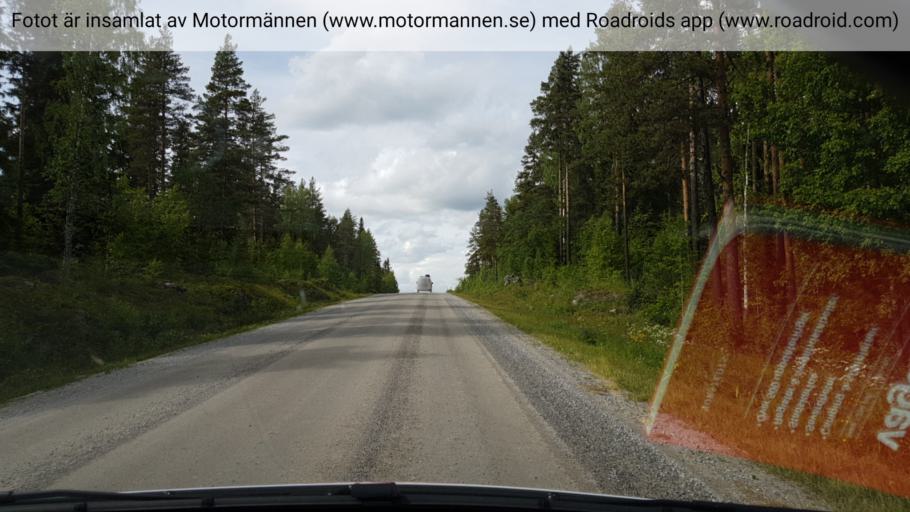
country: SE
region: Vaesternorrland
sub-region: Solleftea Kommun
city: Solleftea
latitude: 63.3150
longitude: 17.2481
